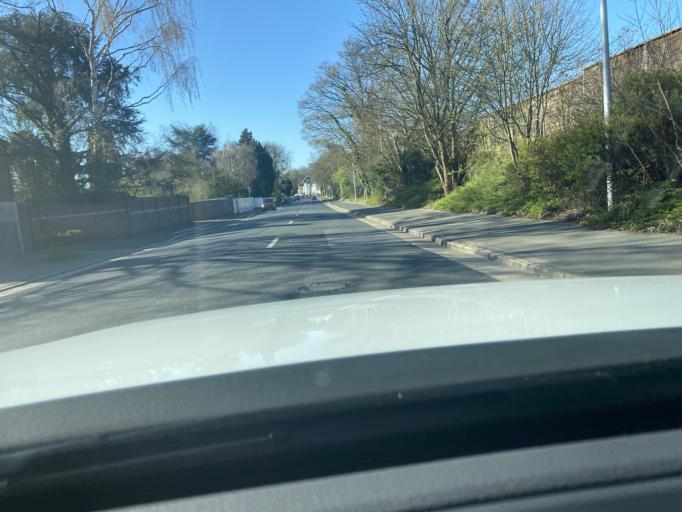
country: DE
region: North Rhine-Westphalia
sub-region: Regierungsbezirk Dusseldorf
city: Ratingen
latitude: 51.2525
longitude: 6.8621
